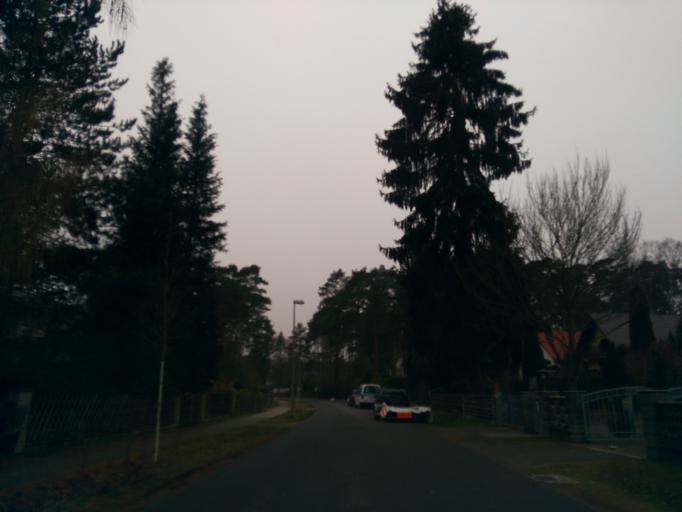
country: DE
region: Brandenburg
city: Falkensee
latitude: 52.5840
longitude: 13.0878
